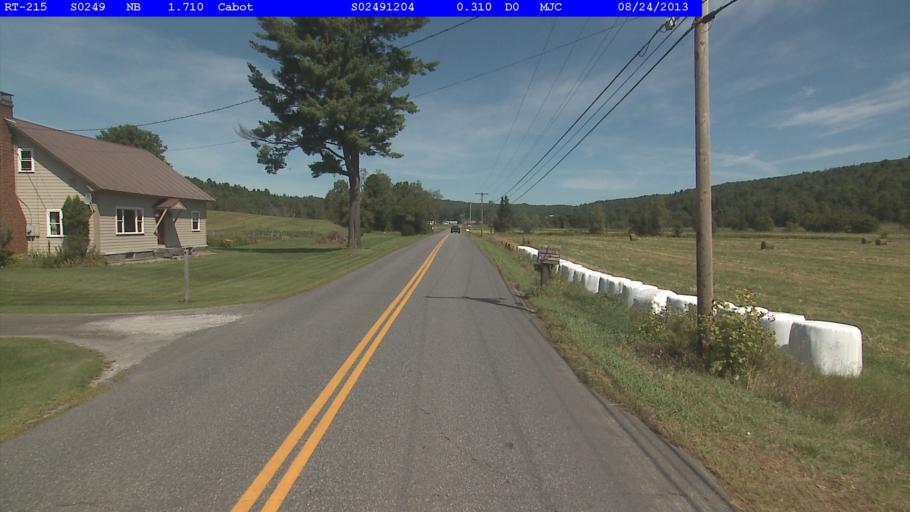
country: US
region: Vermont
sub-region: Caledonia County
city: Hardwick
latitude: 44.3719
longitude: -72.3363
